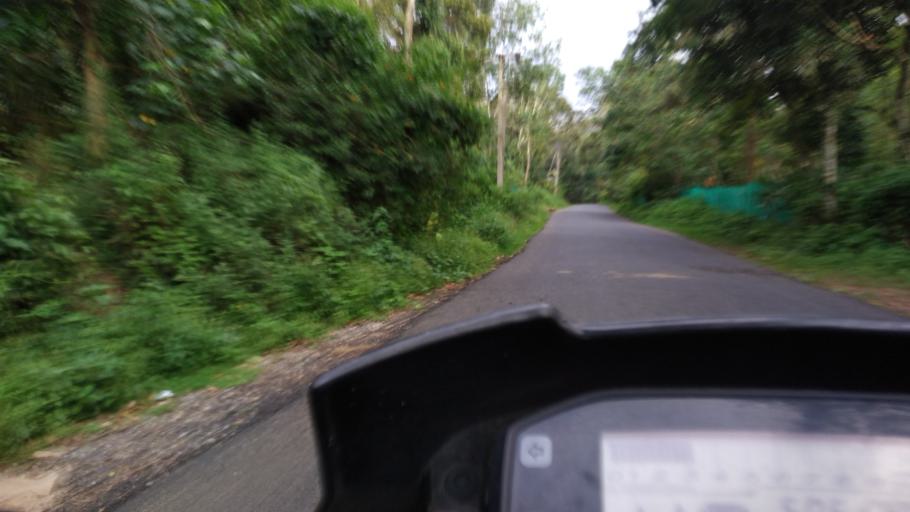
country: IN
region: Tamil Nadu
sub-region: Theni
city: Bodinayakkanur
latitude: 10.0363
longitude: 77.2220
